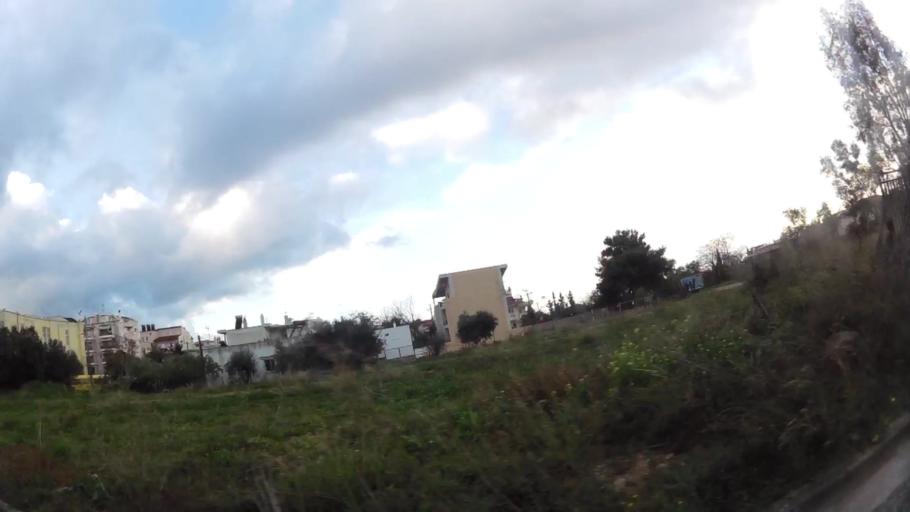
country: GR
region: Attica
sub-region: Nomarchia Athinas
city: Vrilissia
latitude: 38.0421
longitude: 23.8284
